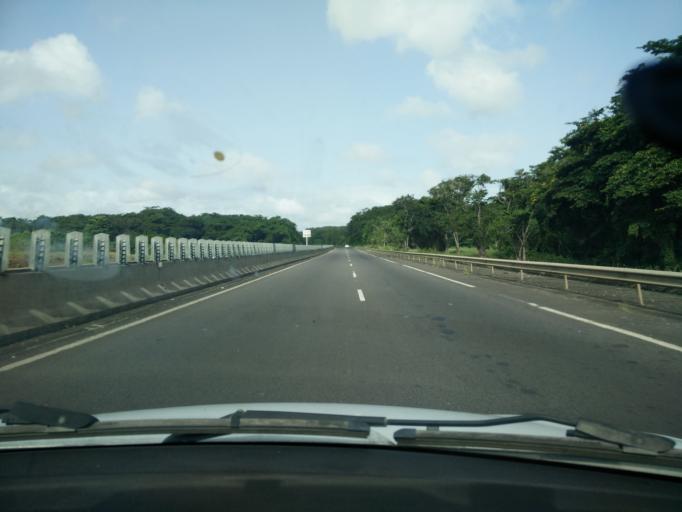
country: GP
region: Guadeloupe
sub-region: Guadeloupe
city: Les Abymes
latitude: 16.2763
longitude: -61.5269
